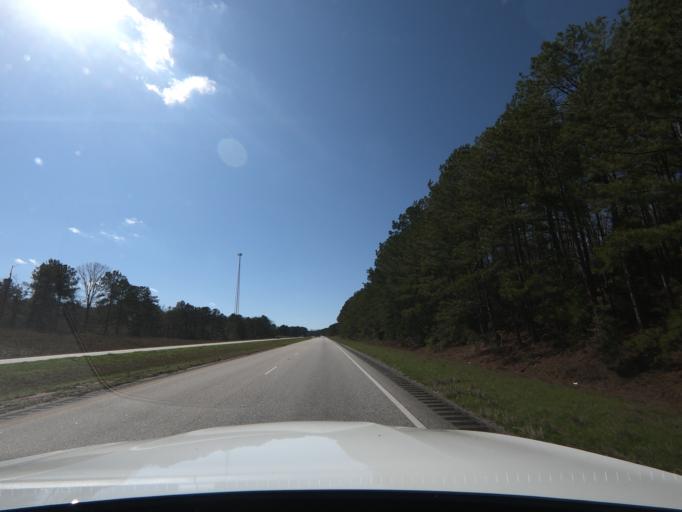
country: US
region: Alabama
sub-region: Henry County
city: Abbeville
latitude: 31.7442
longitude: -85.2405
